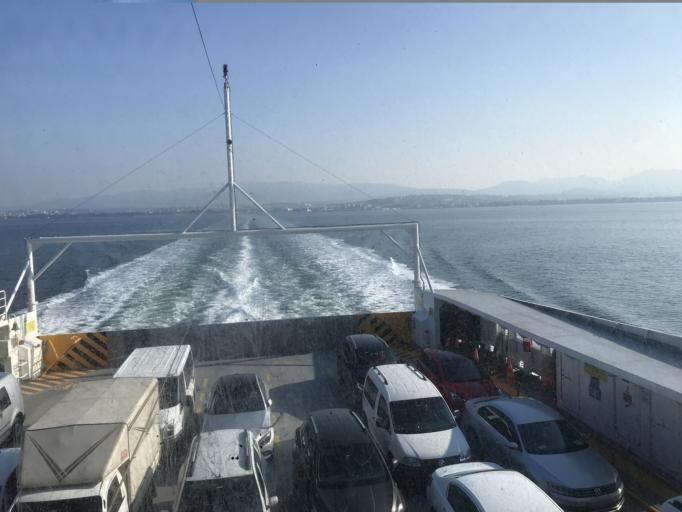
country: TR
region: Yalova
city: Yalova
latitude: 40.6836
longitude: 29.2624
